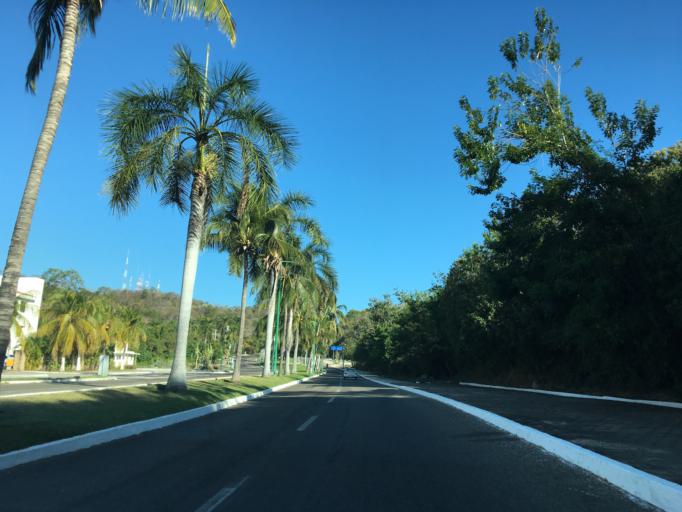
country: MX
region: Oaxaca
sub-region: Santa Maria Huatulco
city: Crucecita
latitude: 15.7669
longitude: -96.1171
